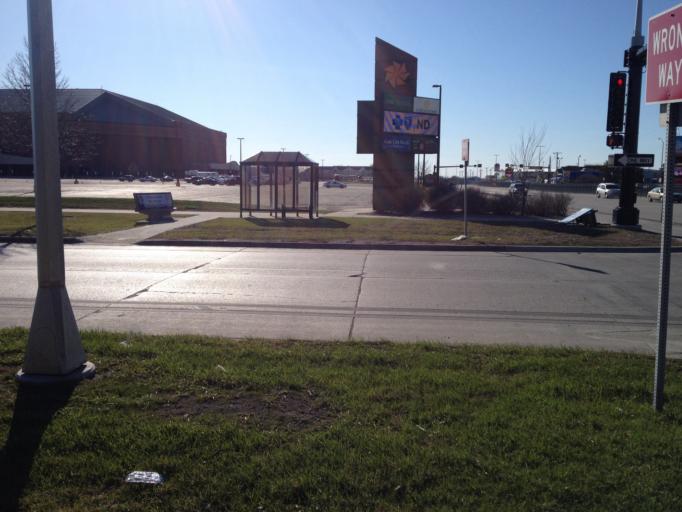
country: US
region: North Dakota
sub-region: Cass County
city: Fargo
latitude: 46.9045
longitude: -96.7979
